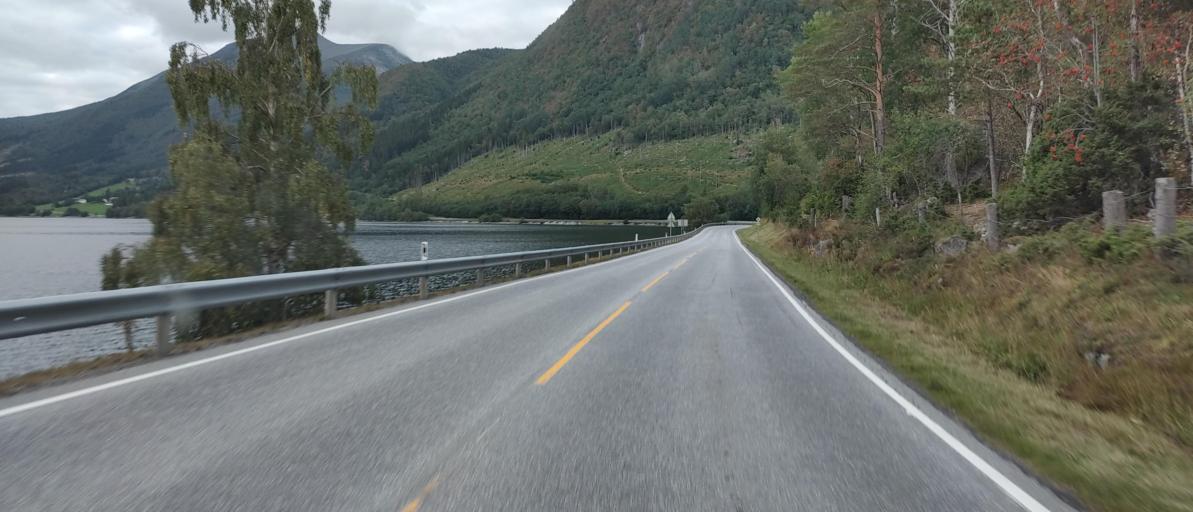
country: NO
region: More og Romsdal
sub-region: Rauma
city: Andalsnes
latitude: 62.5875
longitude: 7.5373
